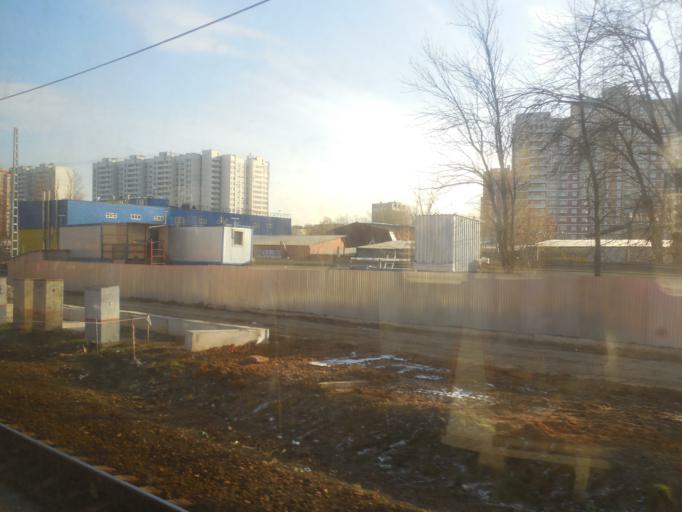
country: RU
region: Moskovskaya
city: Saltykovka
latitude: 55.7526
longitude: 37.9520
